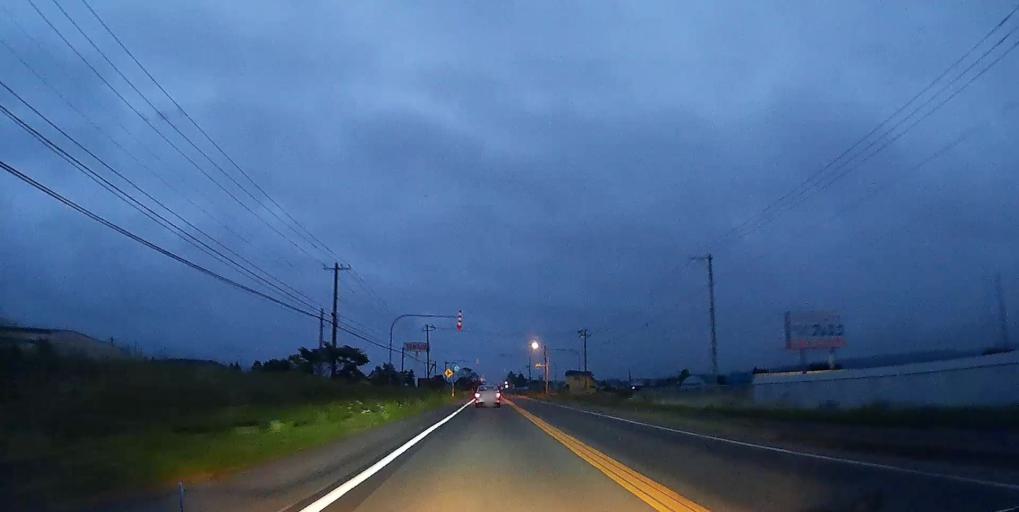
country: JP
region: Hokkaido
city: Nanae
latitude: 42.2207
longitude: 140.3744
